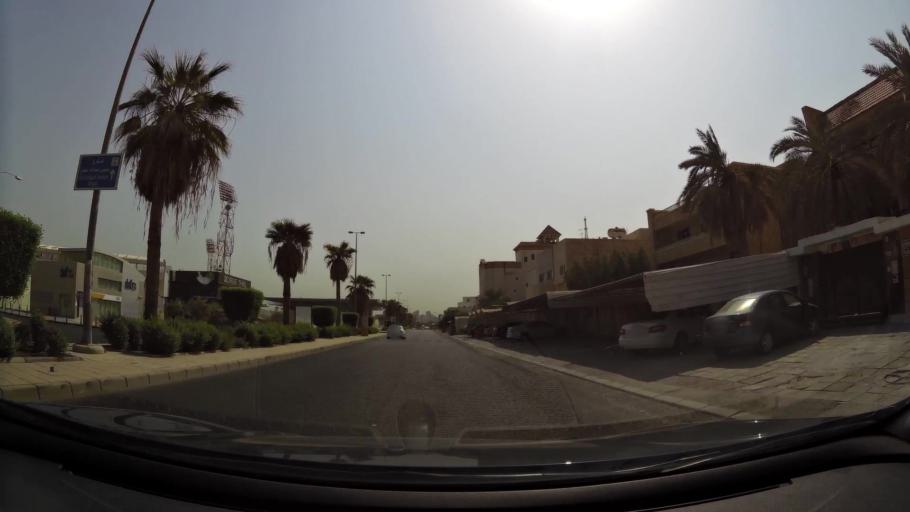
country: KW
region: Al Asimah
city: Ad Dasmah
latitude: 29.3575
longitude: 47.9976
